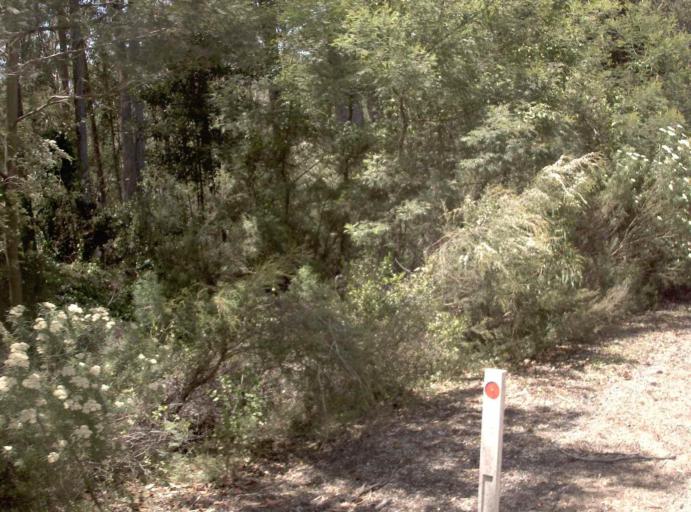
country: AU
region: Victoria
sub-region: East Gippsland
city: Lakes Entrance
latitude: -37.6276
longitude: 147.8869
